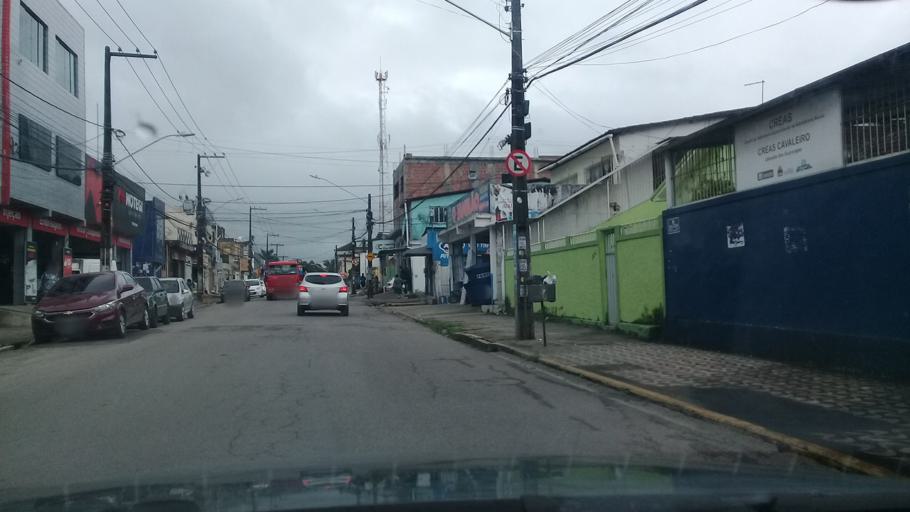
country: BR
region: Pernambuco
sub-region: Jaboatao Dos Guararapes
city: Jaboatao dos Guararapes
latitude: -8.0980
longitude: -34.9713
